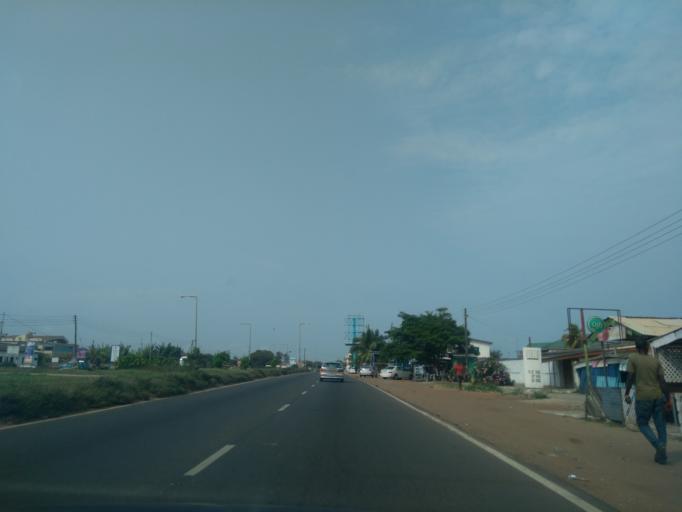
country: GH
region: Greater Accra
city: Accra
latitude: 5.5551
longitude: -0.1702
